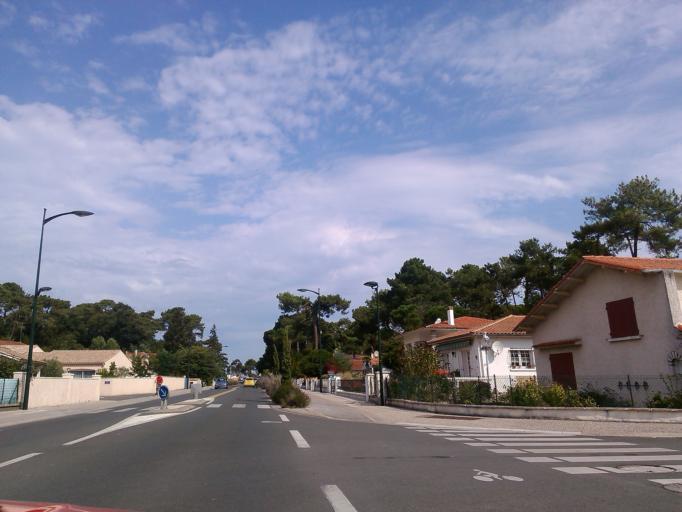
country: FR
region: Poitou-Charentes
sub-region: Departement de la Charente-Maritime
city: La Tremblade
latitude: 45.7904
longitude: -1.1596
